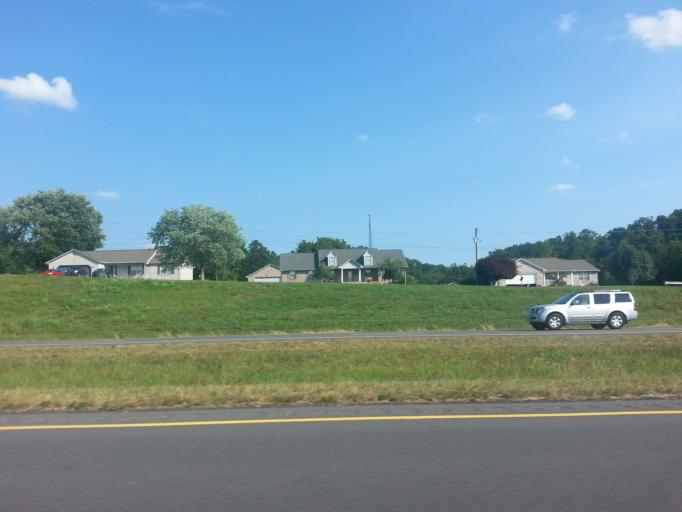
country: US
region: Tennessee
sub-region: Loudon County
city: Greenback
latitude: 35.7523
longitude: -84.1420
